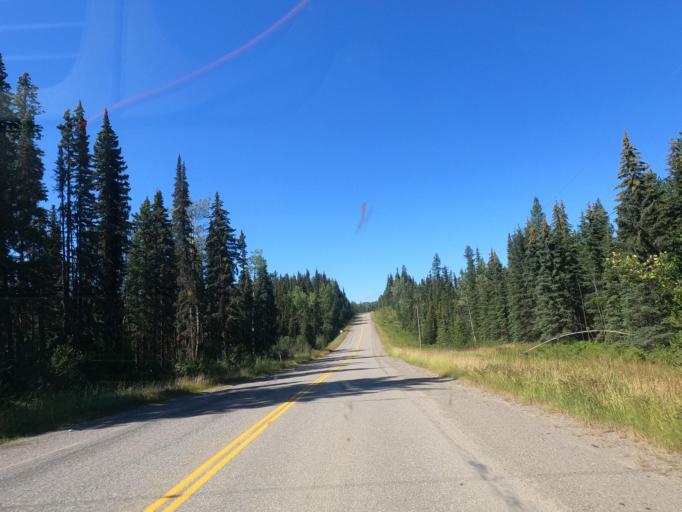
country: CA
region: British Columbia
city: Quesnel
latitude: 53.0337
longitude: -122.2648
